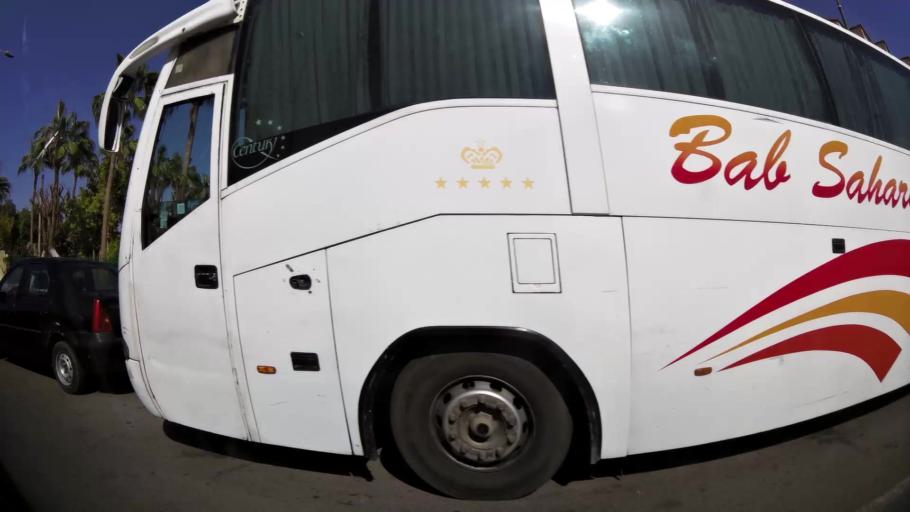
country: MA
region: Souss-Massa-Draa
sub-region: Inezgane-Ait Mellou
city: Inezgane
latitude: 30.3691
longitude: -9.5326
